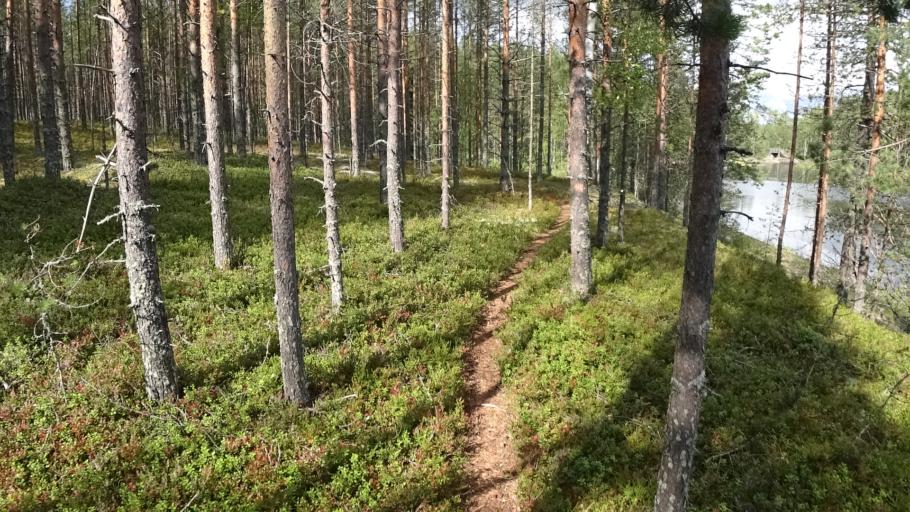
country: FI
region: North Karelia
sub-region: Joensuu
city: Ilomantsi
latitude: 62.6081
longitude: 31.1876
